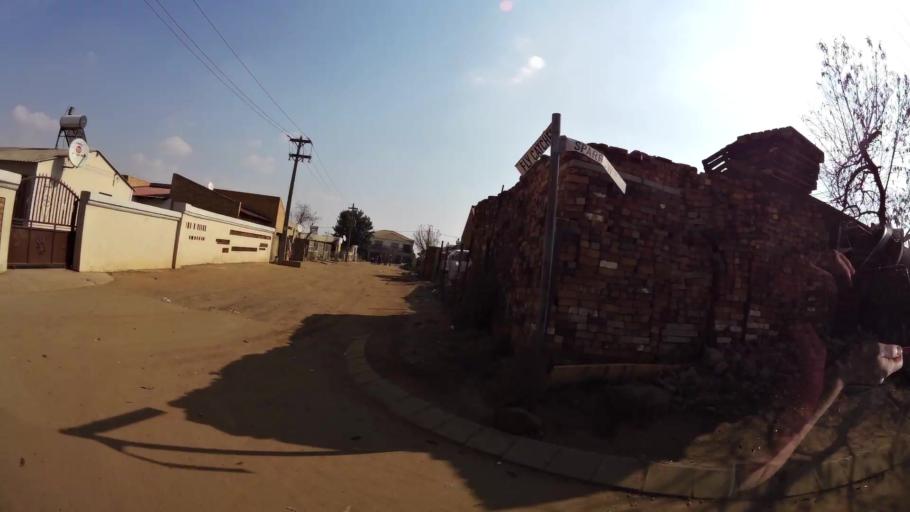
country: ZA
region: Gauteng
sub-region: Ekurhuleni Metropolitan Municipality
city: Springs
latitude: -26.1114
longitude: 28.4779
